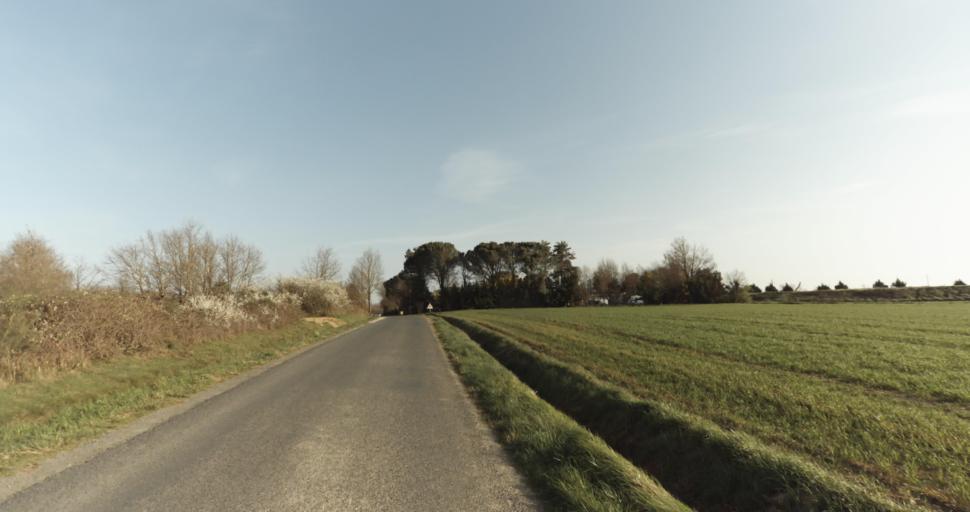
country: FR
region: Midi-Pyrenees
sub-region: Departement du Tarn
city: Saint-Sulpice-la-Pointe
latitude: 43.7448
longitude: 1.6871
